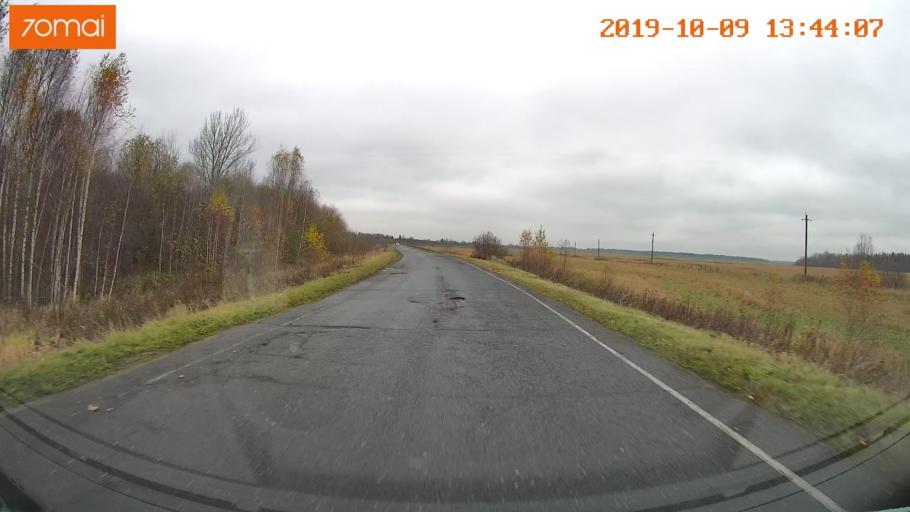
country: RU
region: Kostroma
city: Buy
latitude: 58.3640
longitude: 41.2068
